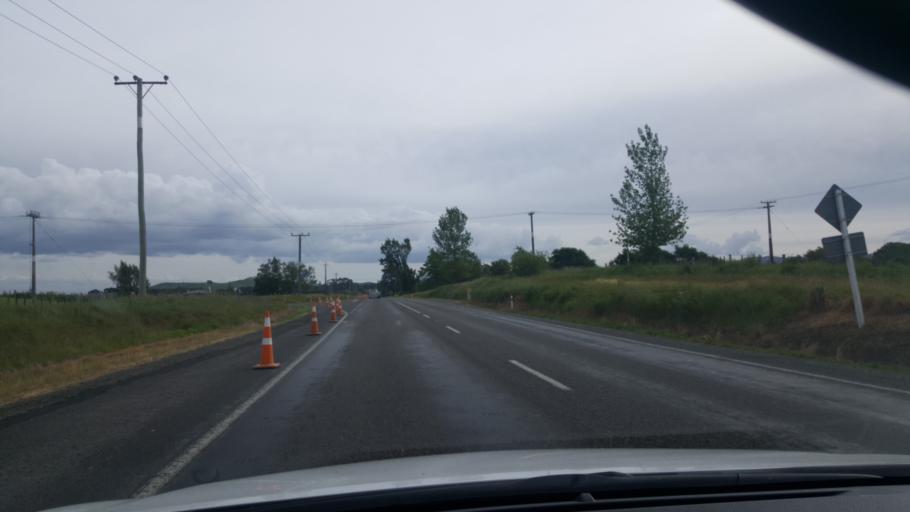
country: NZ
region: Bay of Plenty
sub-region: Rotorua District
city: Rotorua
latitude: -38.4037
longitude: 176.3286
